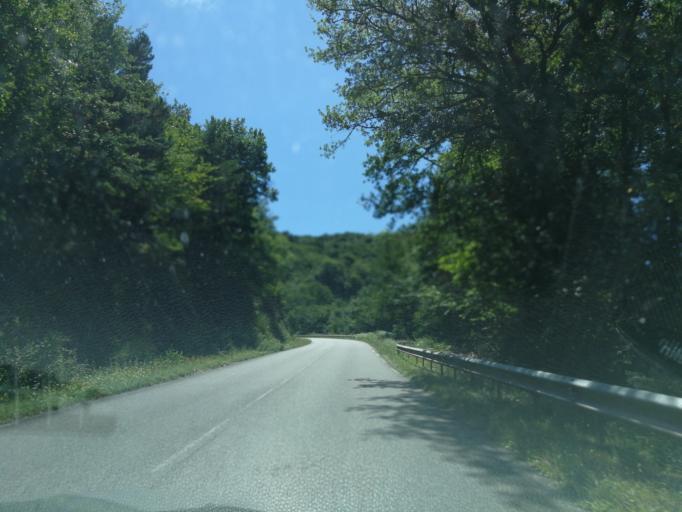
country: FR
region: Limousin
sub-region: Departement de la Correze
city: Argentat
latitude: 45.0680
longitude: 1.9465
